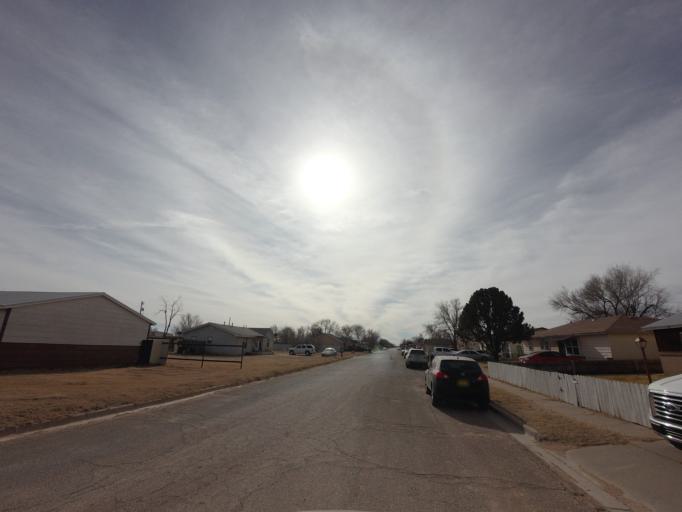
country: US
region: New Mexico
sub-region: Curry County
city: Clovis
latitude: 34.4118
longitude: -103.2375
